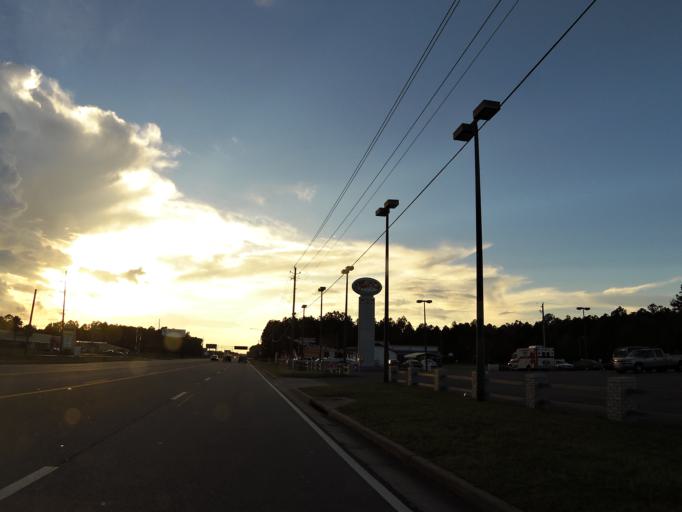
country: US
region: Georgia
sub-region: Camden County
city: St Marys
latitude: 30.7815
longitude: -81.6289
